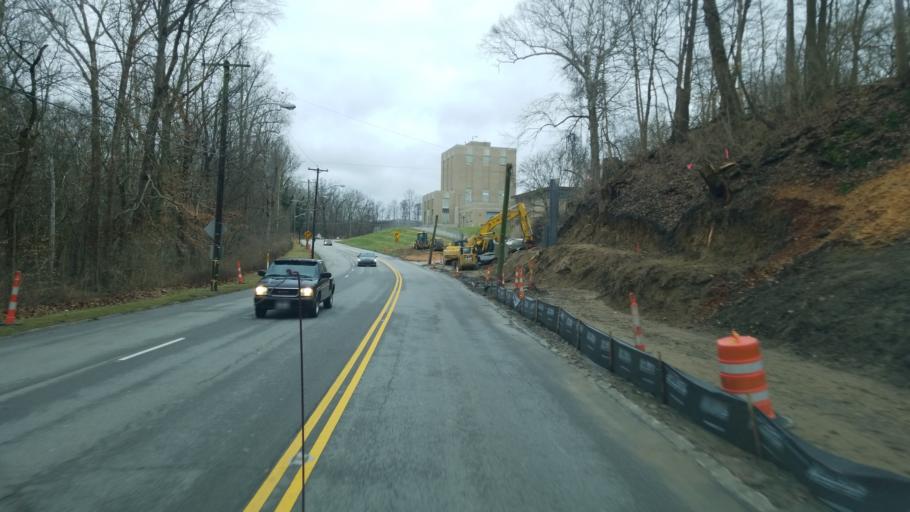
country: US
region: Kentucky
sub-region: Campbell County
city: Fort Thomas
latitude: 39.0755
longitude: -84.4206
